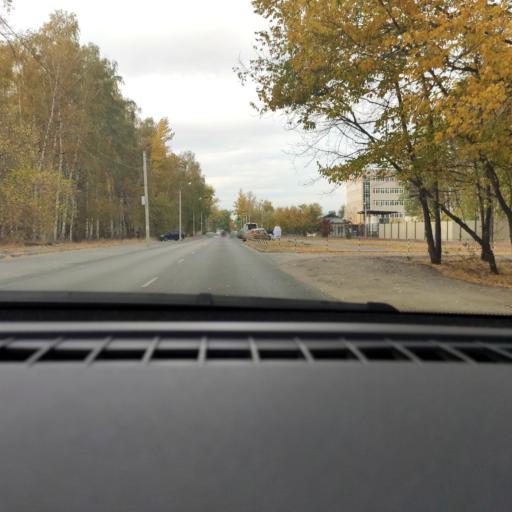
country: RU
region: Voronezj
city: Podgornoye
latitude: 51.7394
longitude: 39.1765
